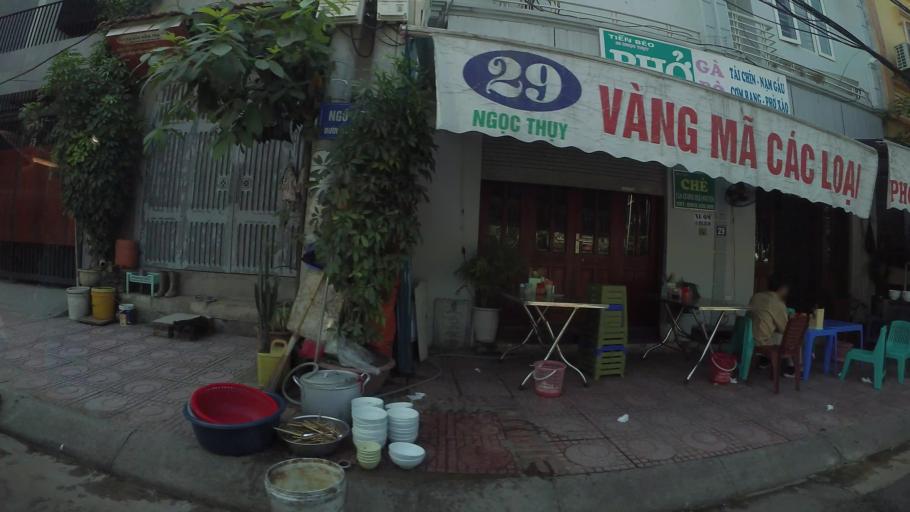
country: VN
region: Ha Noi
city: Hoan Kiem
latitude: 21.0635
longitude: 105.8704
